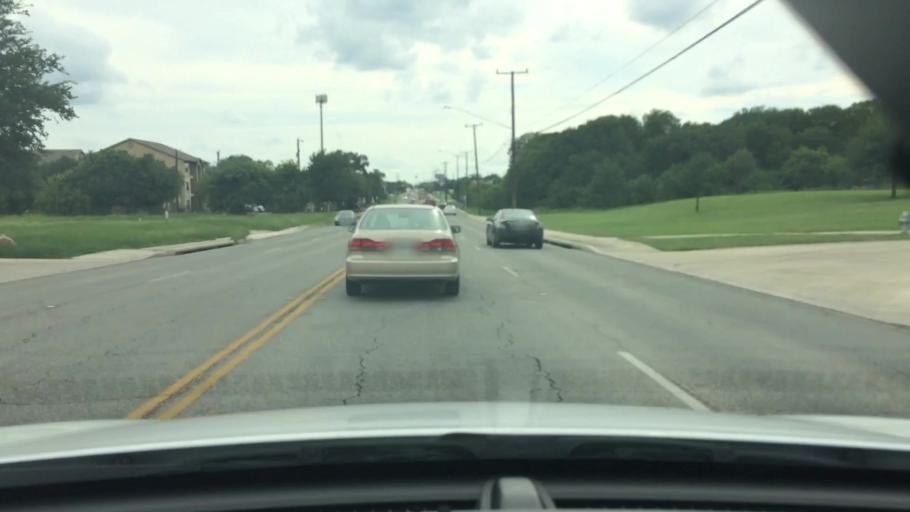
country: US
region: Texas
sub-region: Bexar County
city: Leon Valley
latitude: 29.5162
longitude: -98.6073
